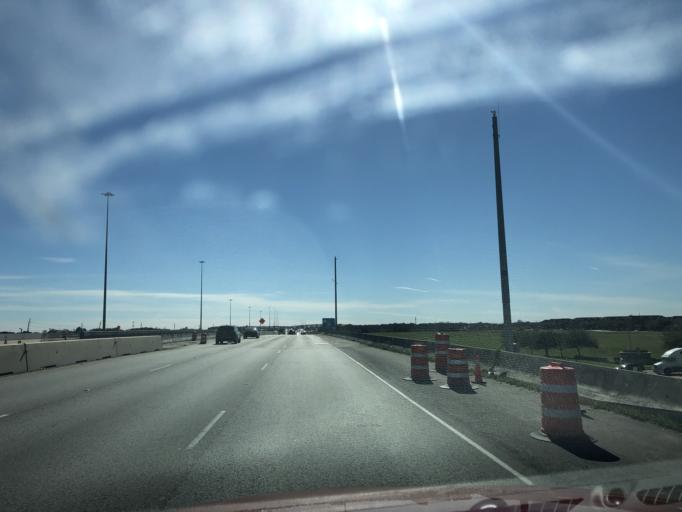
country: US
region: Texas
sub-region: Brazoria County
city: Brookside Village
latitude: 29.6286
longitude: -95.3873
